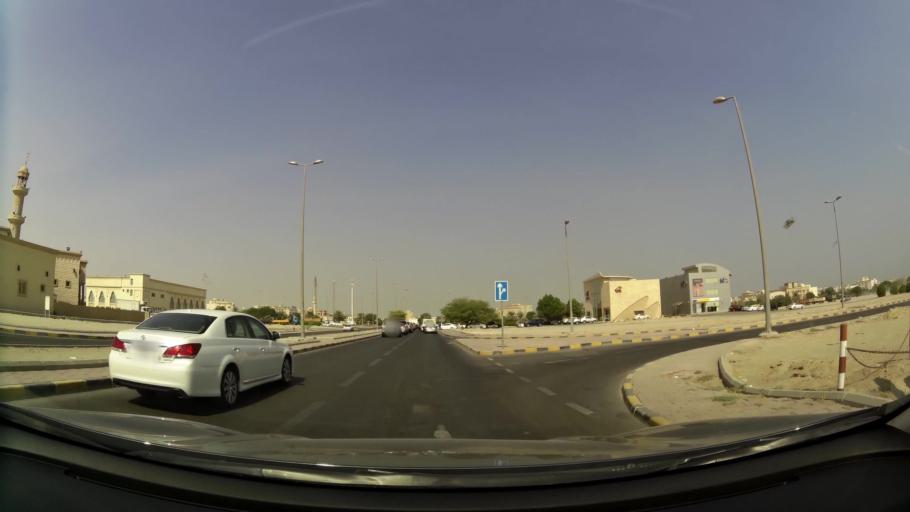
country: KW
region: Al Ahmadi
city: Al Ahmadi
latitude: 29.0902
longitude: 48.1058
